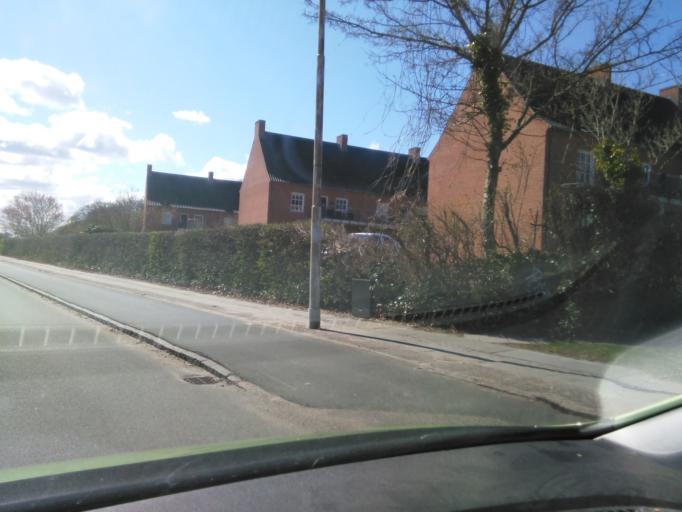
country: DK
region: Central Jutland
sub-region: Arhus Kommune
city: Arhus
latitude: 56.1875
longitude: 10.2379
